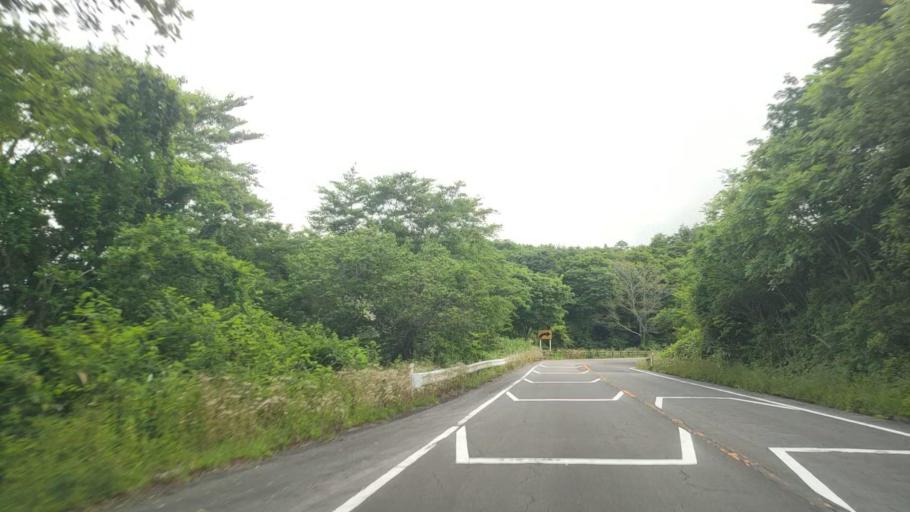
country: JP
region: Tottori
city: Kurayoshi
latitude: 35.3279
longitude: 133.5897
